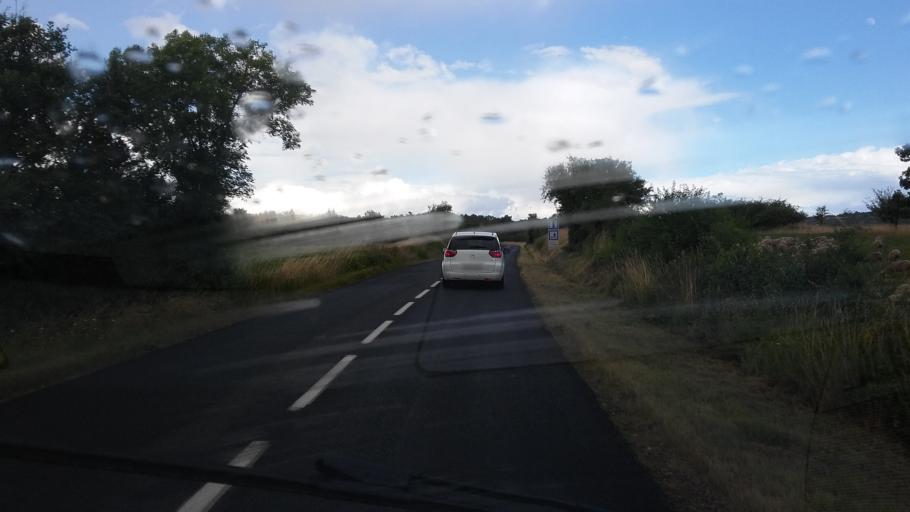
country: FR
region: Midi-Pyrenees
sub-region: Departement de l'Aveyron
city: La Cavalerie
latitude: 43.9521
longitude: 3.2498
